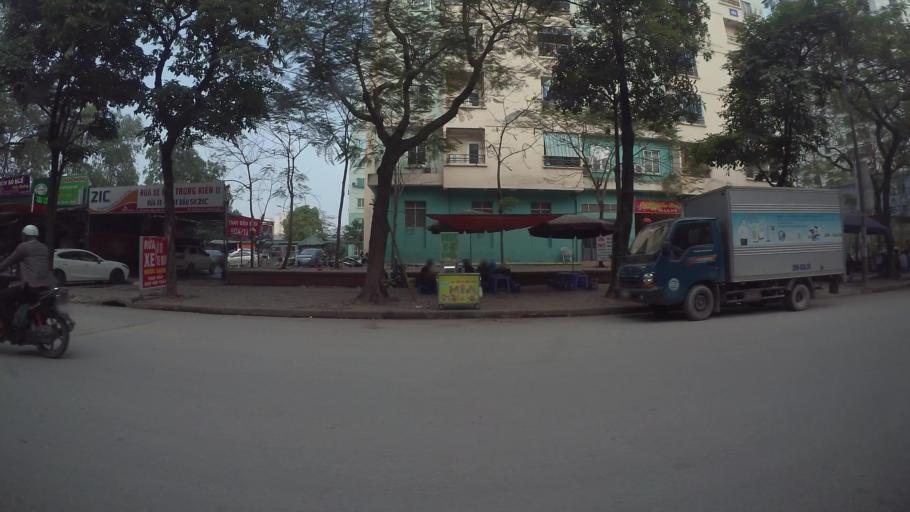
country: VN
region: Ha Noi
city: Van Dien
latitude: 20.9768
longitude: 105.8360
